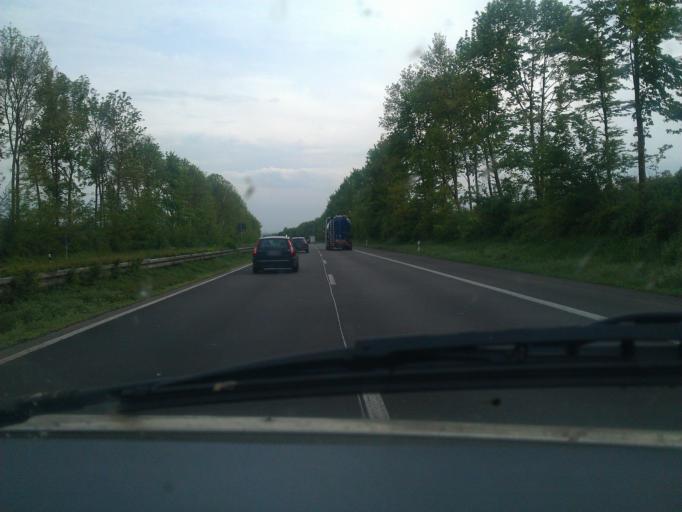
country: DE
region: North Rhine-Westphalia
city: Julich
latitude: 50.9559
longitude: 6.3538
